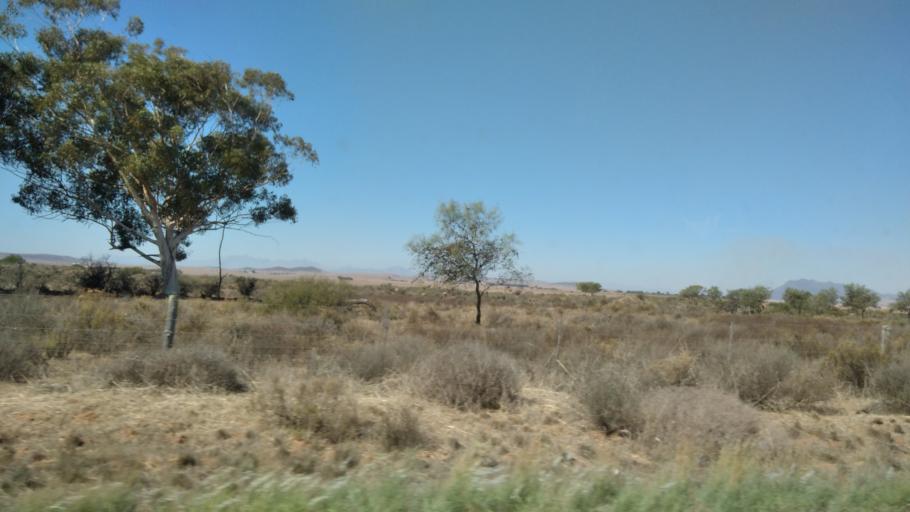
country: ZA
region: Western Cape
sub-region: West Coast District Municipality
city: Moorreesburg
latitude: -33.2717
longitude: 18.6000
